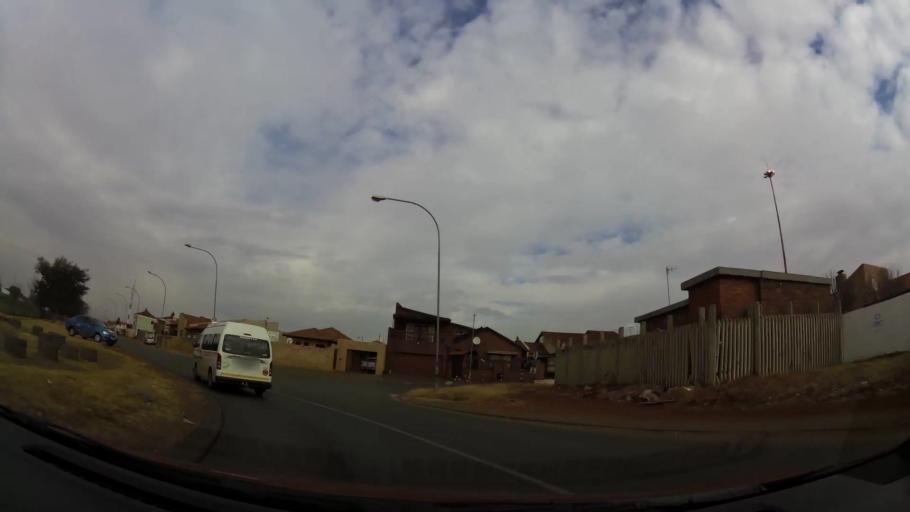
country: ZA
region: Gauteng
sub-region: City of Johannesburg Metropolitan Municipality
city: Soweto
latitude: -26.2716
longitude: 27.8374
